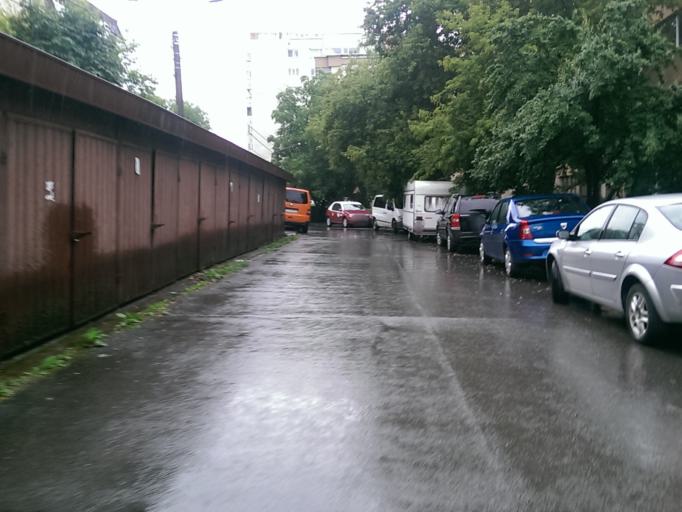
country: RO
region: Cluj
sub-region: Municipiul Cluj-Napoca
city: Cluj-Napoca
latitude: 46.7690
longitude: 23.6104
